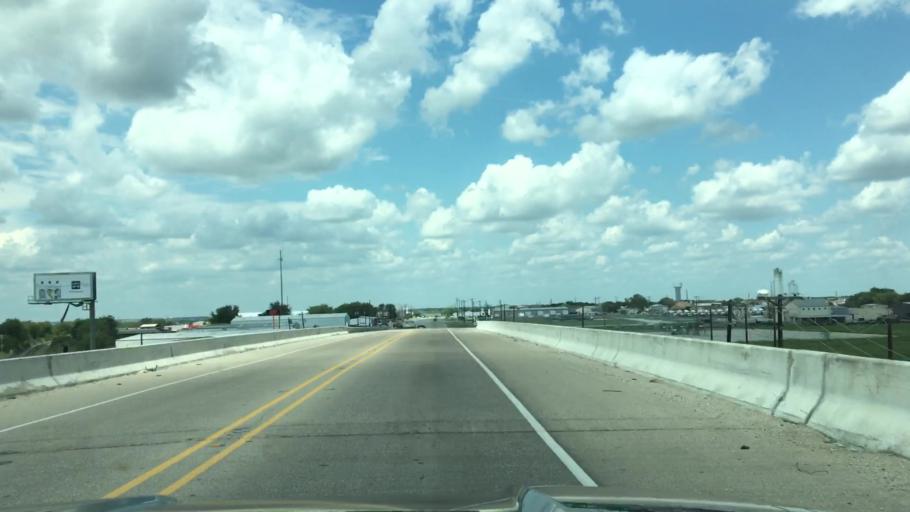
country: US
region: Texas
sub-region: Tarrant County
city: Eagle Mountain
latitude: 32.9449
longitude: -97.4208
